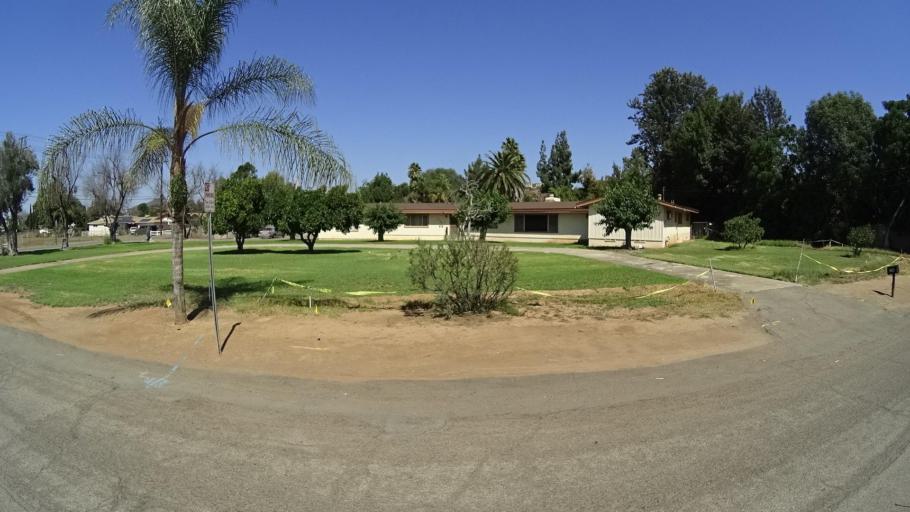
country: US
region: California
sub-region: San Diego County
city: Granite Hills
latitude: 32.8014
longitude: -116.9176
